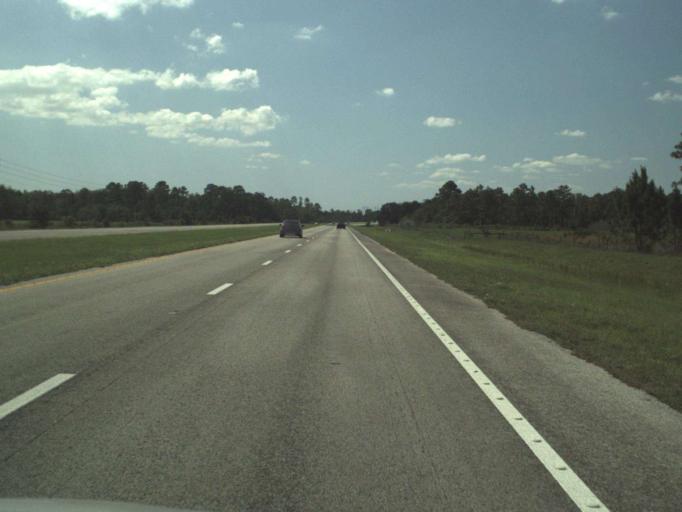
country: US
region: Florida
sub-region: Orange County
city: Wedgefield
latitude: 28.4869
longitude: -81.0357
